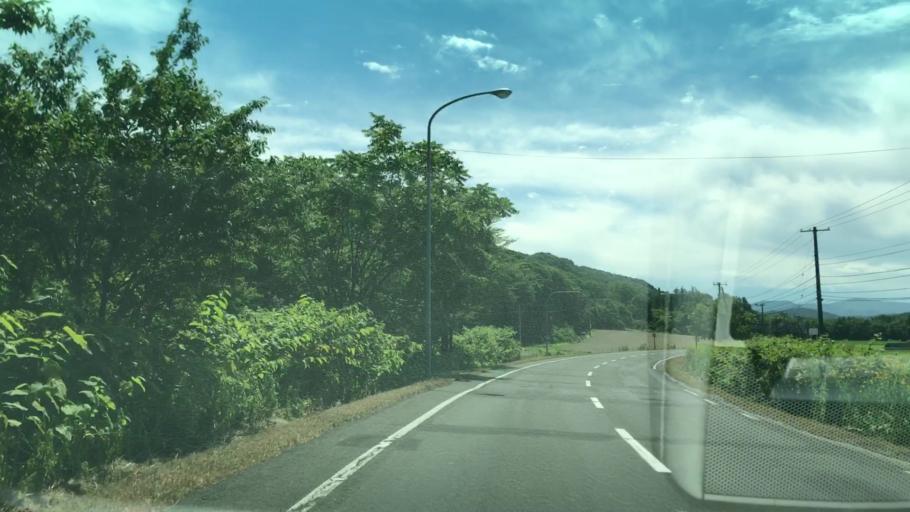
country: JP
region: Hokkaido
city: Shimo-furano
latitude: 42.9750
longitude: 142.4189
